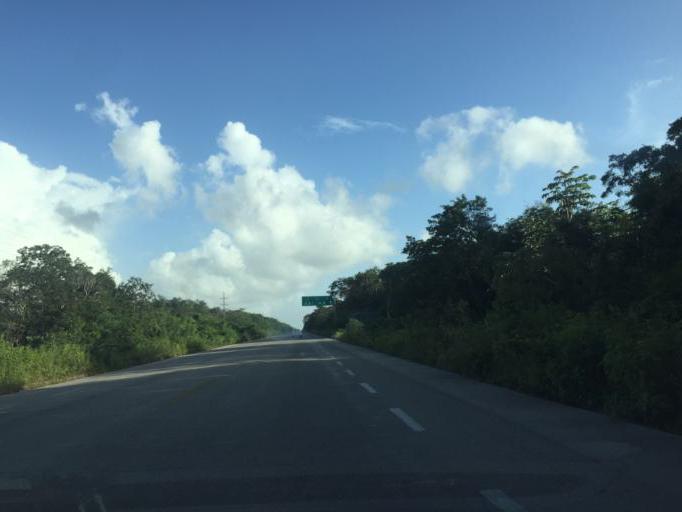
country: MX
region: Quintana Roo
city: Coba
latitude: 20.4891
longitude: -87.7023
